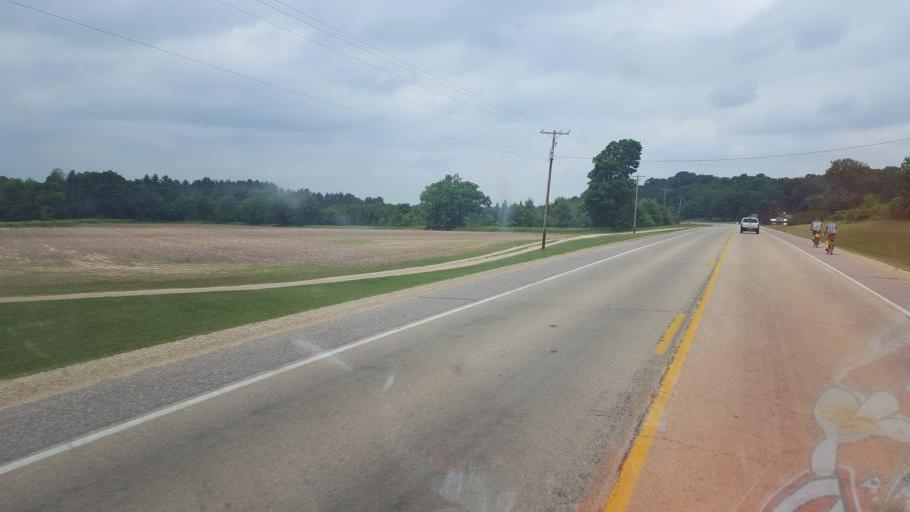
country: US
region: Wisconsin
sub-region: Juneau County
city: Elroy
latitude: 43.6309
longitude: -90.1726
